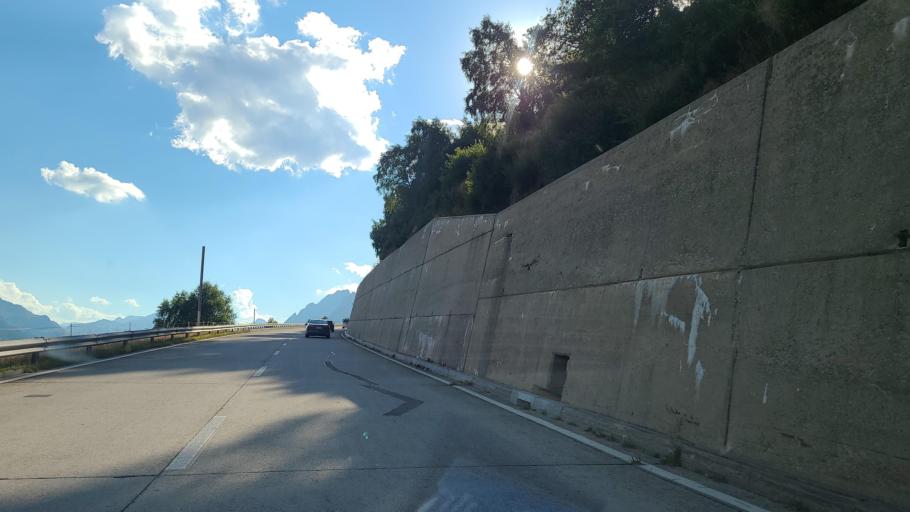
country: CH
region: Ticino
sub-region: Leventina District
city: Airolo
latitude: 46.5291
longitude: 8.5694
